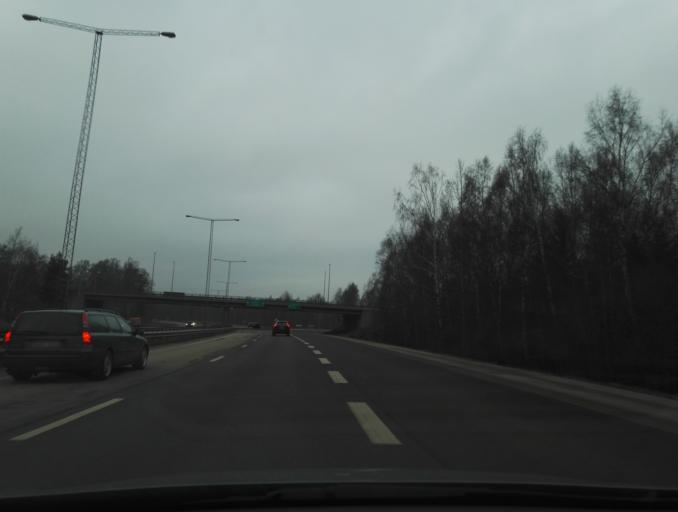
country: SE
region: Kronoberg
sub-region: Vaxjo Kommun
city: Vaexjoe
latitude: 56.8888
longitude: 14.7551
